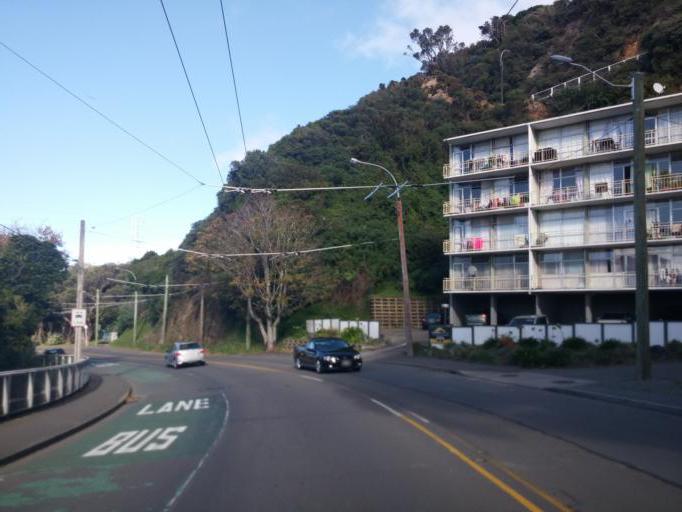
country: NZ
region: Wellington
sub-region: Wellington City
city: Kelburn
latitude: -41.2837
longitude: 174.7522
